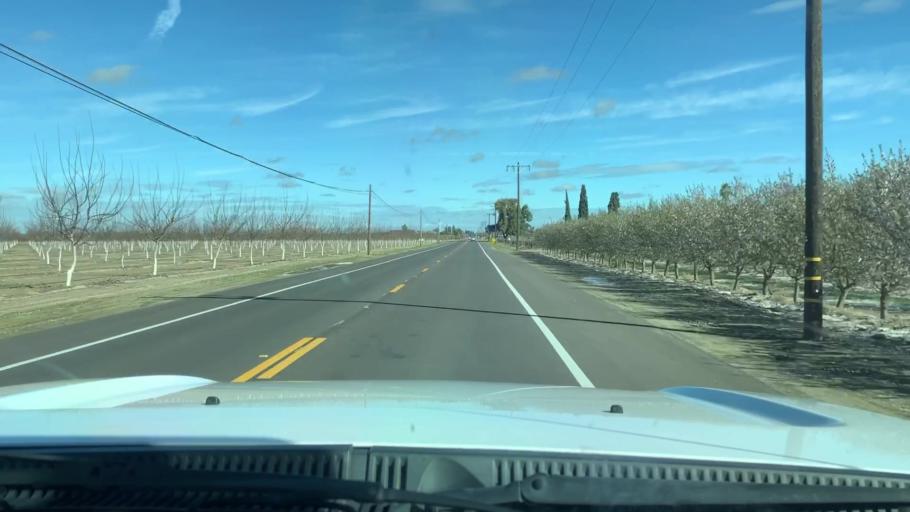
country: US
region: California
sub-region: Fresno County
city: Selma
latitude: 36.5337
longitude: -119.6829
